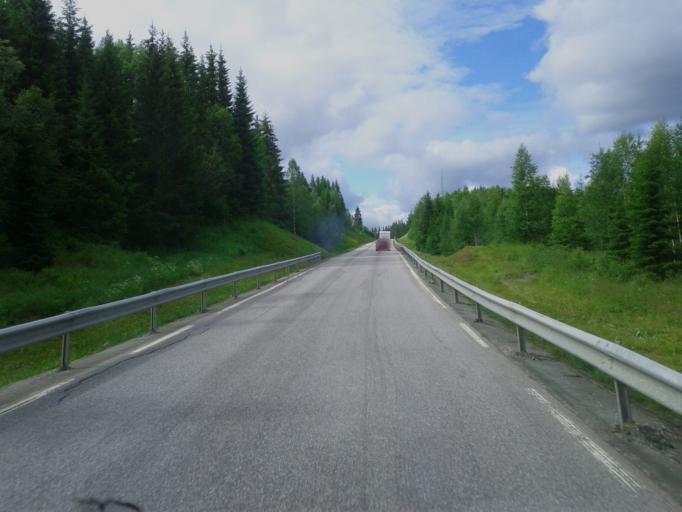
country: NO
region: Nord-Trondelag
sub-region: Hoylandet
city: Hoylandet
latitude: 64.6347
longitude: 12.6150
